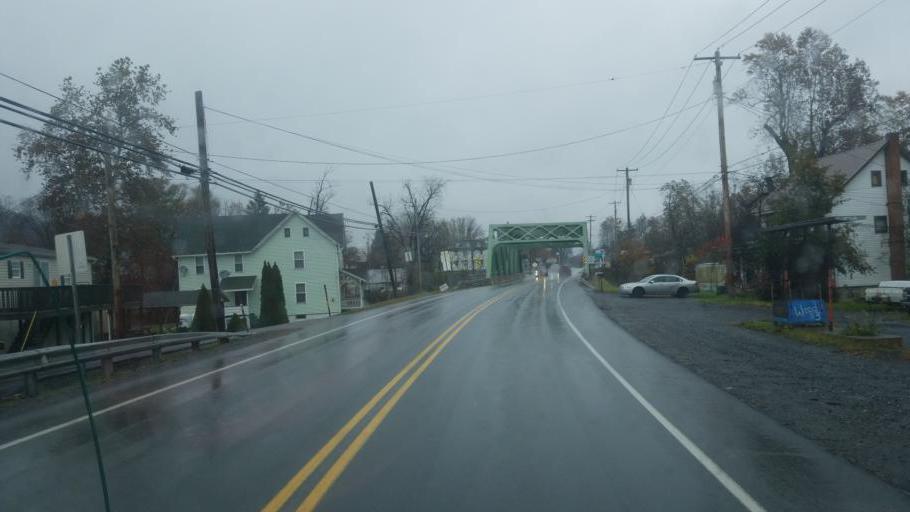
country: US
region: Pennsylvania
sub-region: Clinton County
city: Mill Hall
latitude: 41.0748
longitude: -77.5933
